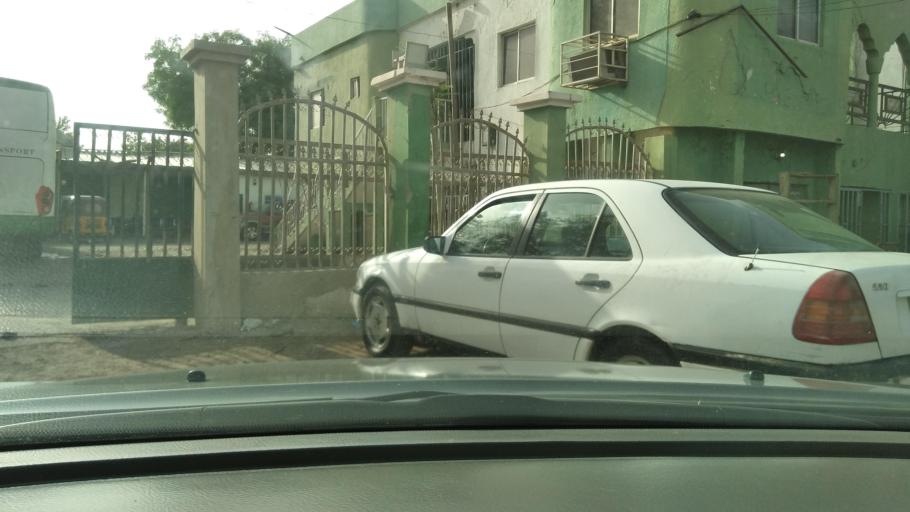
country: NG
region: Kano
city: Kano
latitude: 11.9438
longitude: 8.5649
